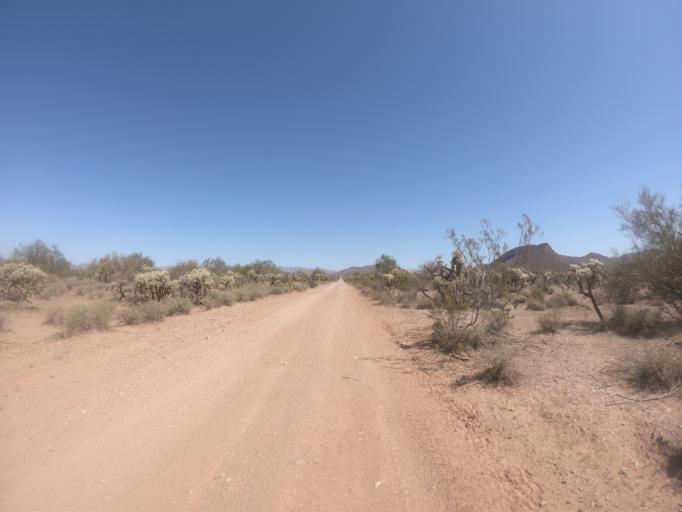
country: US
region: Arizona
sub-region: Pinal County
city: Gold Camp
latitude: 33.2485
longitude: -111.2820
